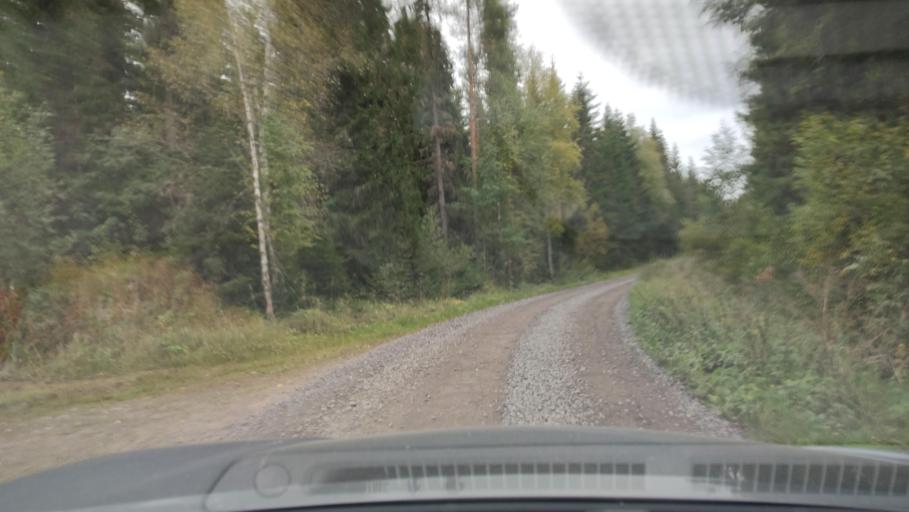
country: FI
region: Southern Ostrobothnia
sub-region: Suupohja
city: Karijoki
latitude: 62.2121
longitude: 21.5728
